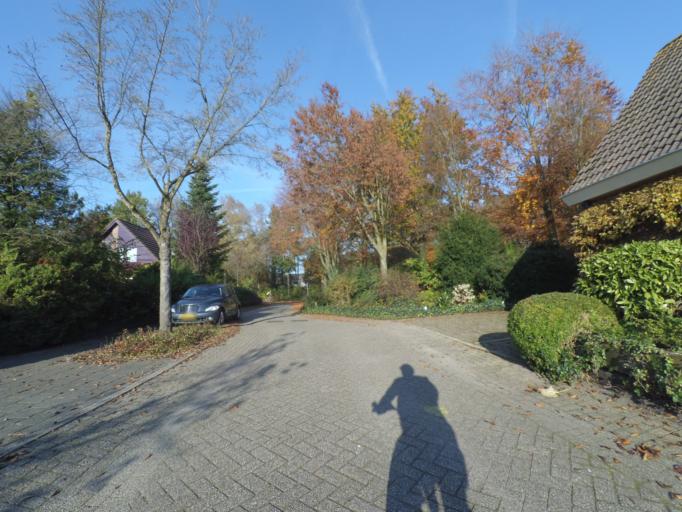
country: NL
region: Utrecht
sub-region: Gemeente Leusden
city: Leusden
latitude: 52.1271
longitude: 5.4453
